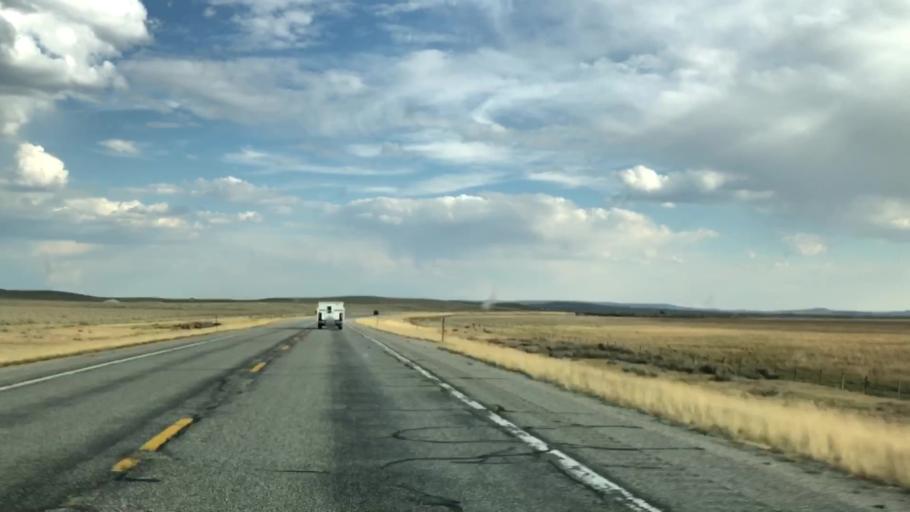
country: US
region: Wyoming
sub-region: Sublette County
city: Pinedale
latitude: 43.0352
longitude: -110.1323
